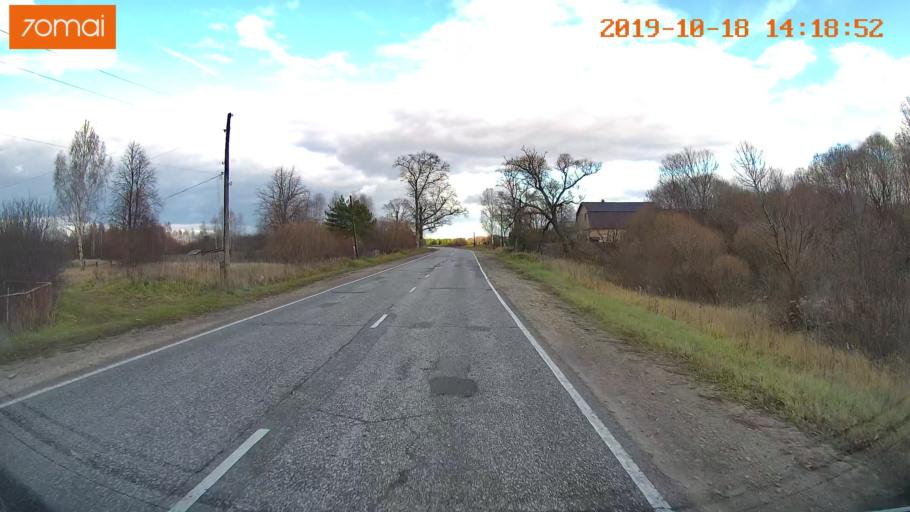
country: RU
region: Rjazan
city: Tuma
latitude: 55.1400
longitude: 40.3994
